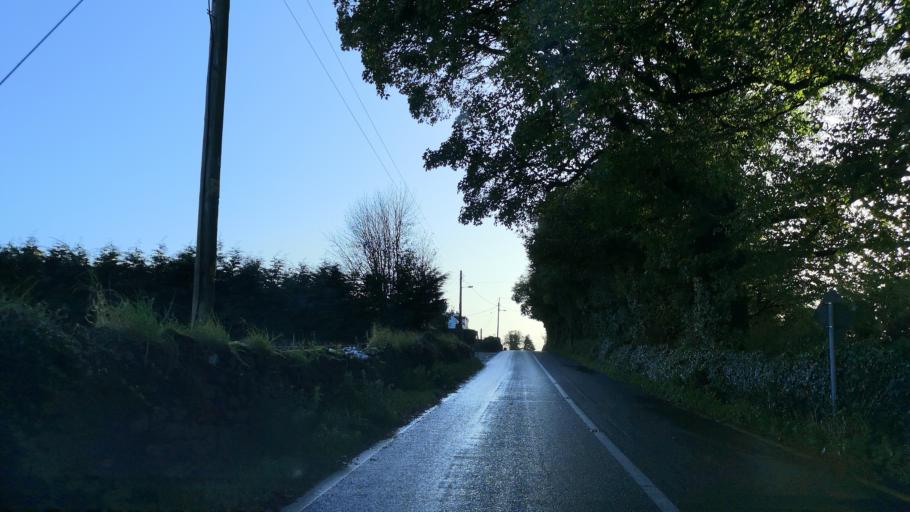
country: IE
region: Connaught
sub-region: Roscommon
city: Castlerea
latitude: 53.7640
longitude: -8.5059
